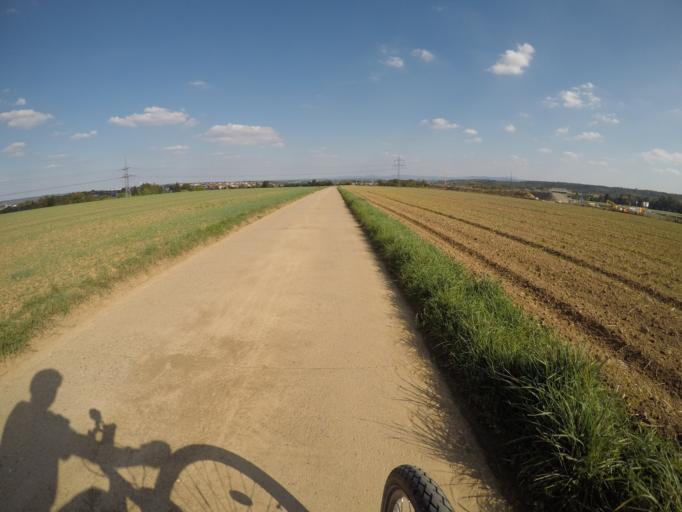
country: DE
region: Baden-Wuerttemberg
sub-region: Regierungsbezirk Stuttgart
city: Neuhausen auf den Fildern
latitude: 48.6953
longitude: 9.2945
